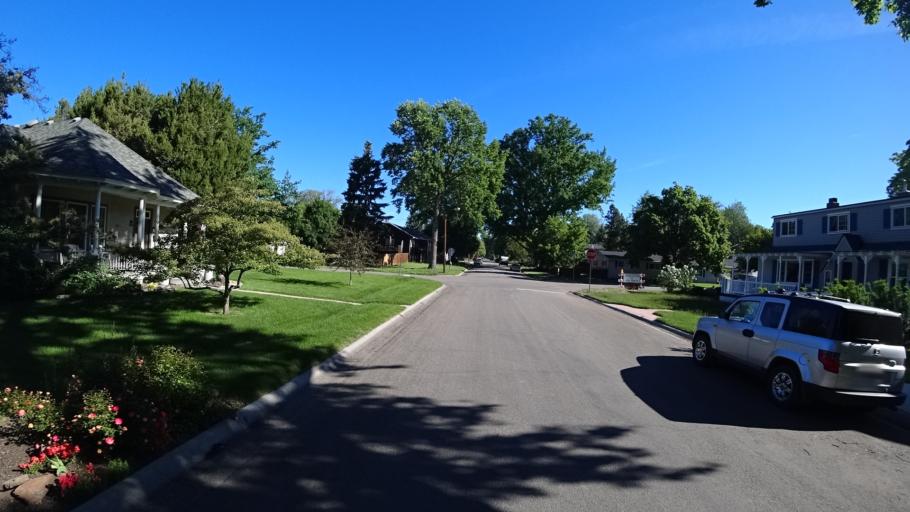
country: US
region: Idaho
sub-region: Ada County
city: Garden City
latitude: 43.6362
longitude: -116.2259
